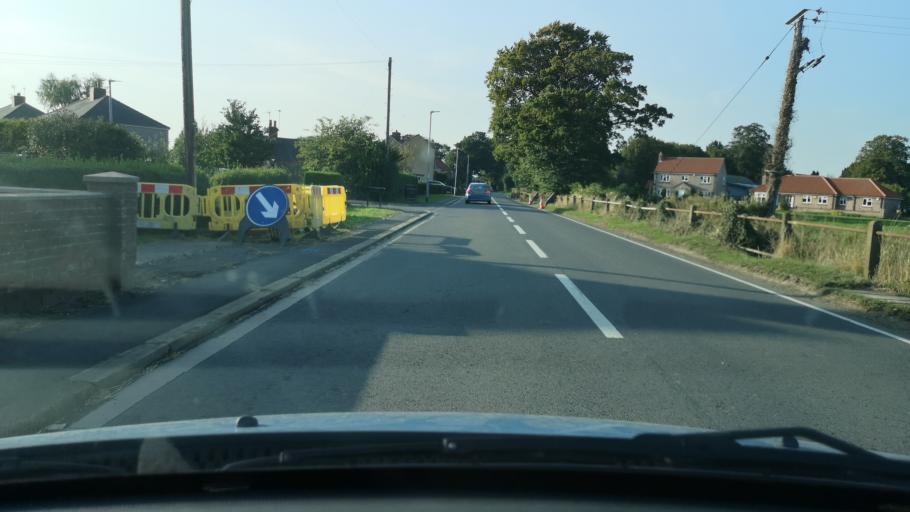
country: GB
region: England
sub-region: East Riding of Yorkshire
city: Skelton
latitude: 53.6885
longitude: -0.8291
